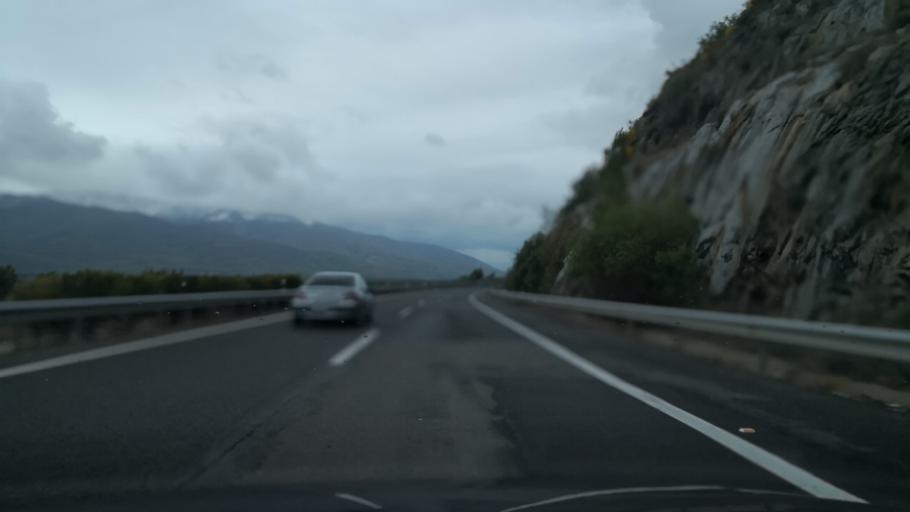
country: ES
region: Extremadura
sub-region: Provincia de Caceres
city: Banos de Montemayor
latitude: 40.2995
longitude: -5.8882
